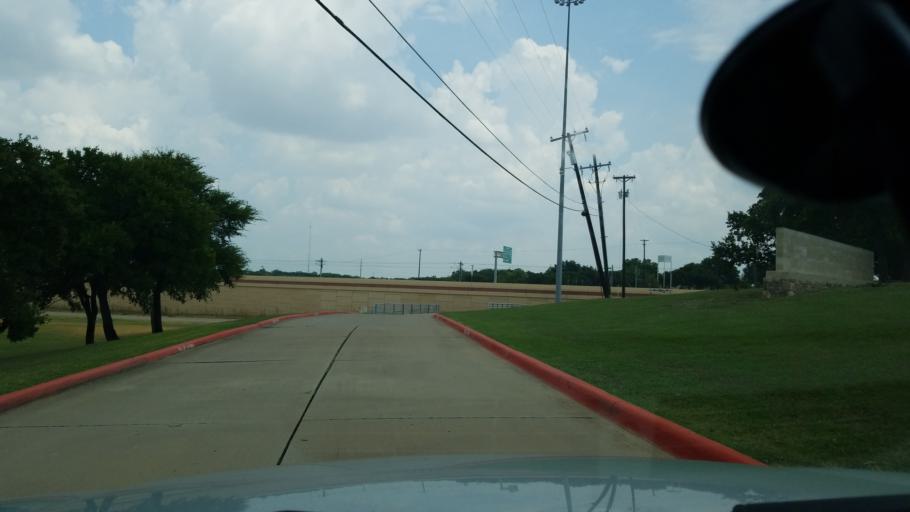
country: US
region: Texas
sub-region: Dallas County
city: Irving
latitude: 32.8512
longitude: -96.9233
